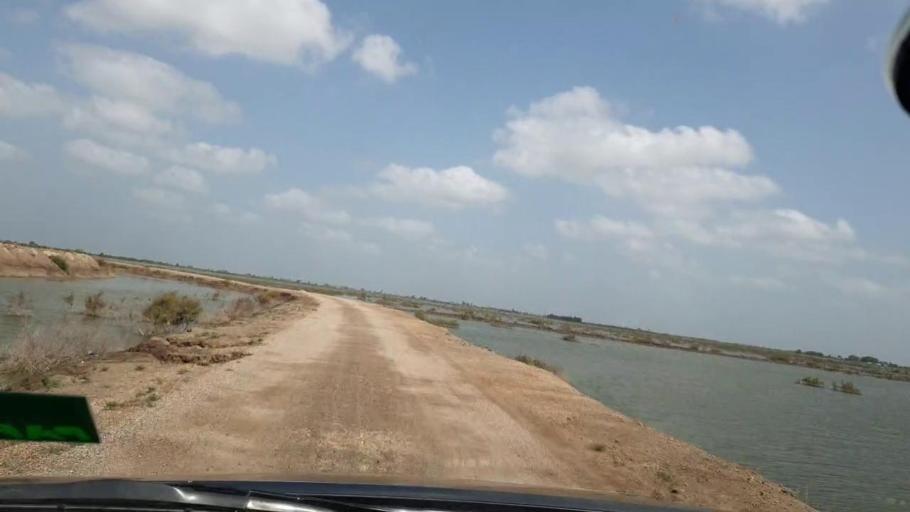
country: PK
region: Sindh
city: Kadhan
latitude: 24.5858
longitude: 69.1395
